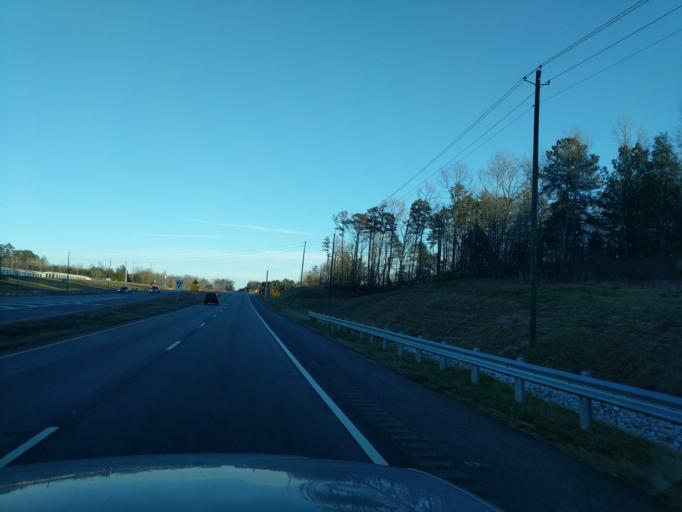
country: US
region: Georgia
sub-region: Stephens County
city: Toccoa
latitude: 34.5235
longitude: -83.2463
